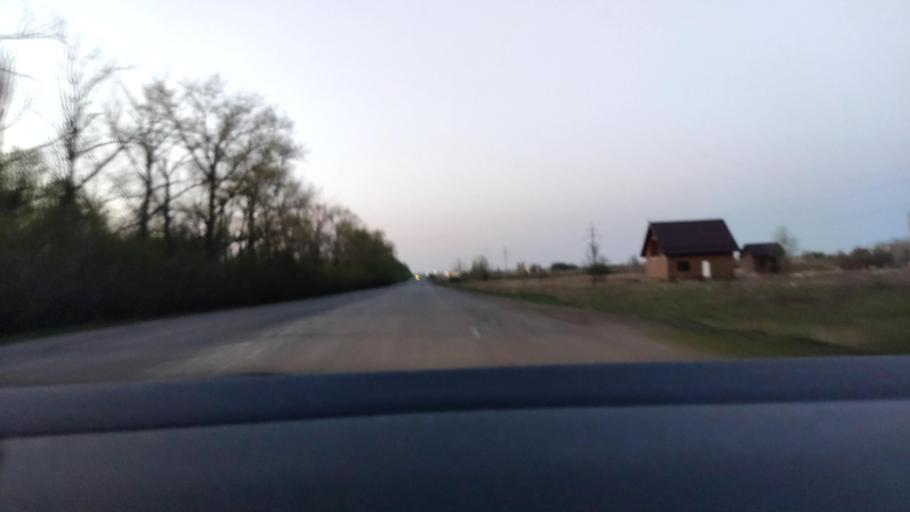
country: RU
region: Voronezj
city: Maslovka
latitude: 51.5153
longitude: 39.3016
